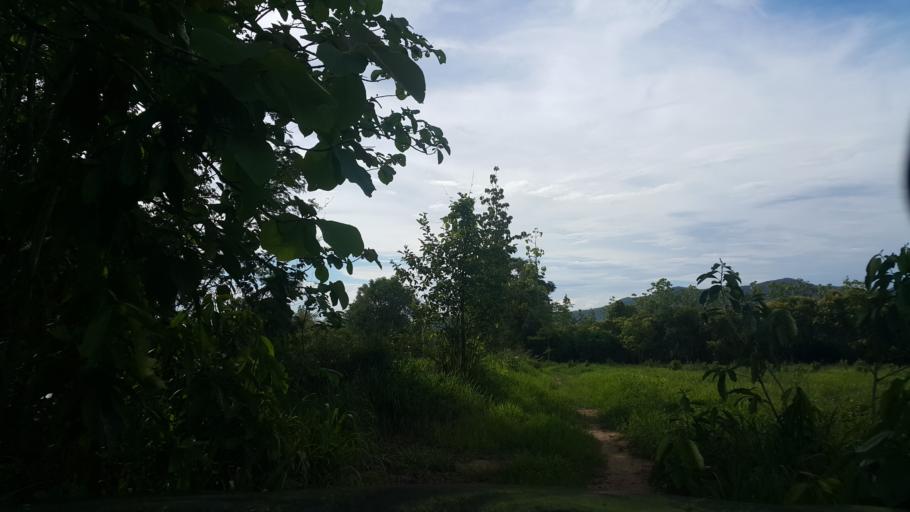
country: TH
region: Chiang Mai
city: Mae On
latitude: 18.7132
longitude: 99.2165
